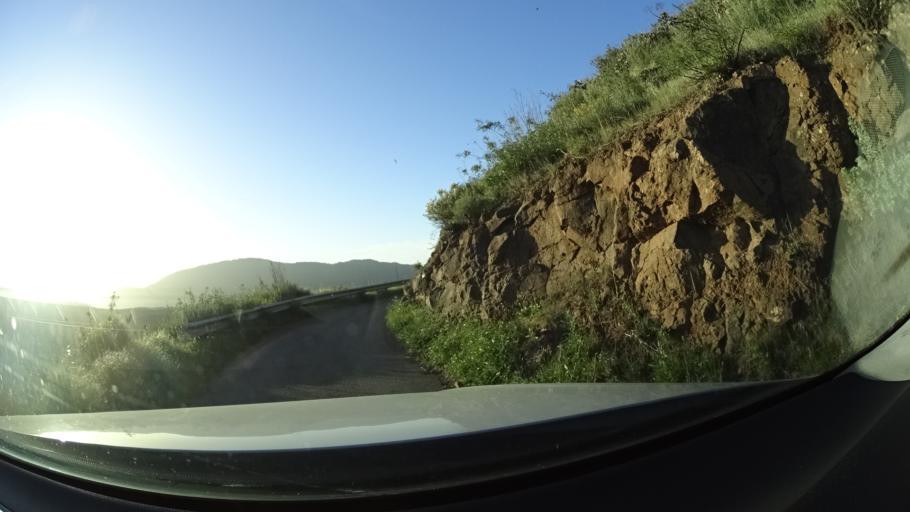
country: ES
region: Canary Islands
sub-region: Provincia de Las Palmas
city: Artenara
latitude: 28.0385
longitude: -15.6468
